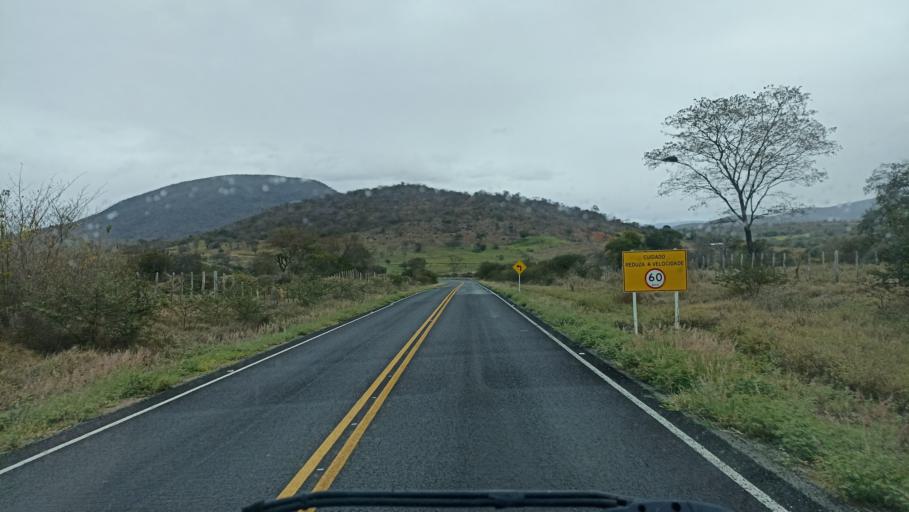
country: BR
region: Bahia
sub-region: Andarai
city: Vera Cruz
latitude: -13.0456
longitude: -40.7705
